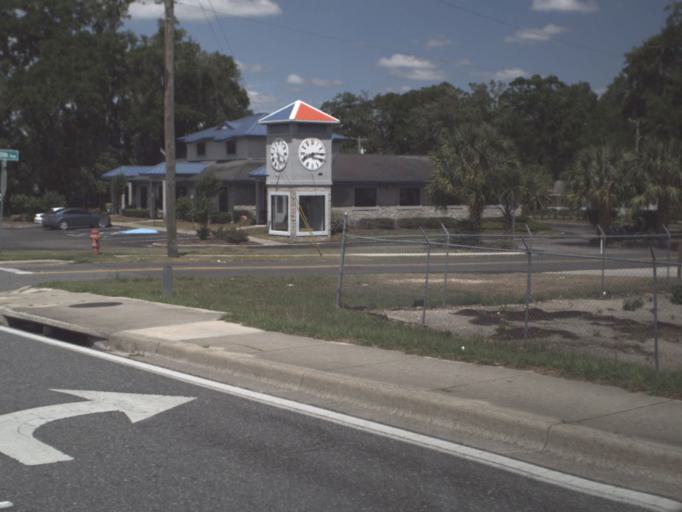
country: US
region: Florida
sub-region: Marion County
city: Ocala
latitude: 29.1791
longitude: -82.1469
